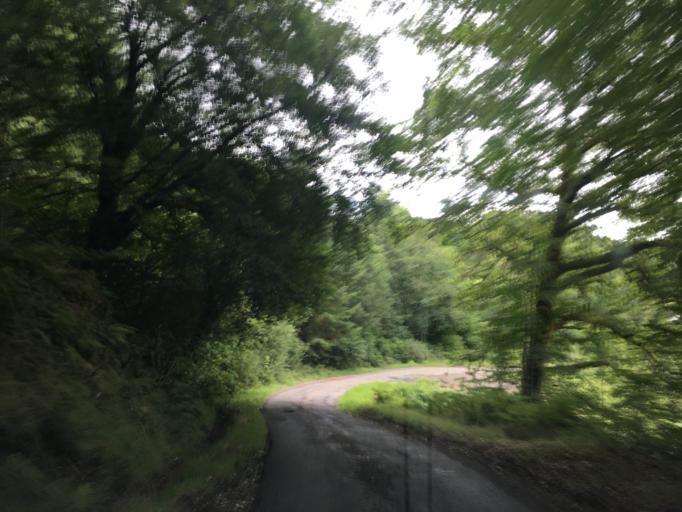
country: GB
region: Scotland
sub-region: Argyll and Bute
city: Oban
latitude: 56.2764
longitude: -5.2811
